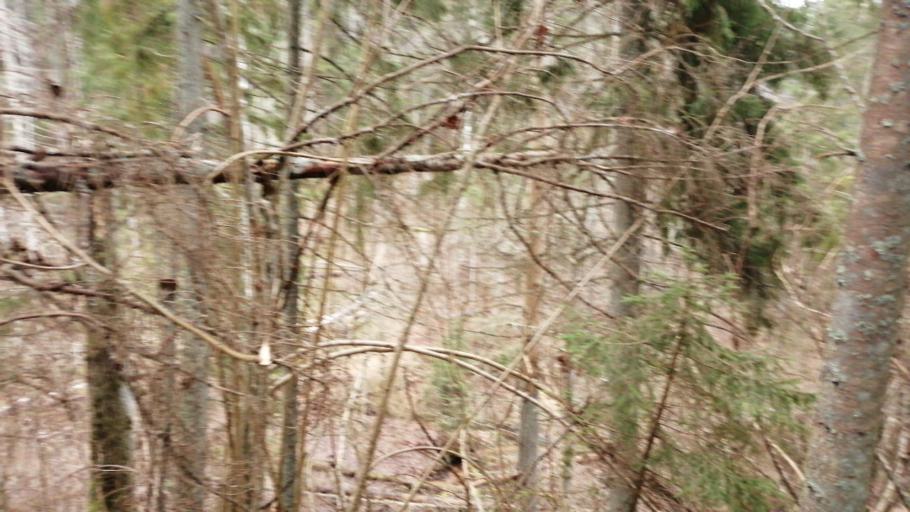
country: EE
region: Polvamaa
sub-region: Polva linn
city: Polva
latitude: 58.0280
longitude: 26.9250
